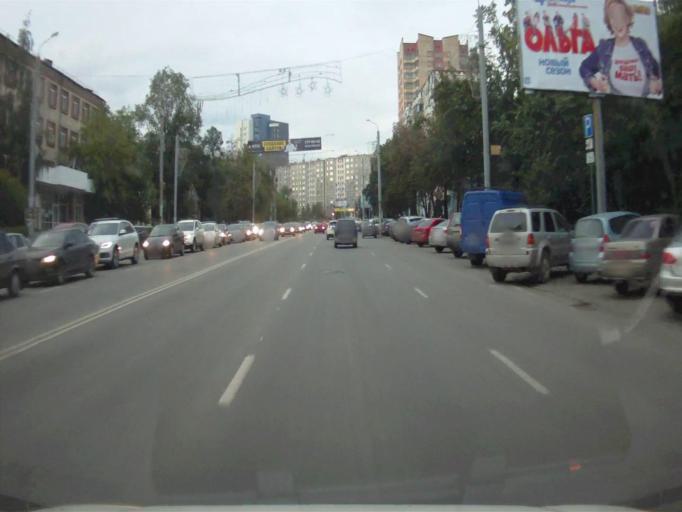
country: RU
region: Chelyabinsk
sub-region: Gorod Chelyabinsk
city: Chelyabinsk
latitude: 55.1559
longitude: 61.3815
